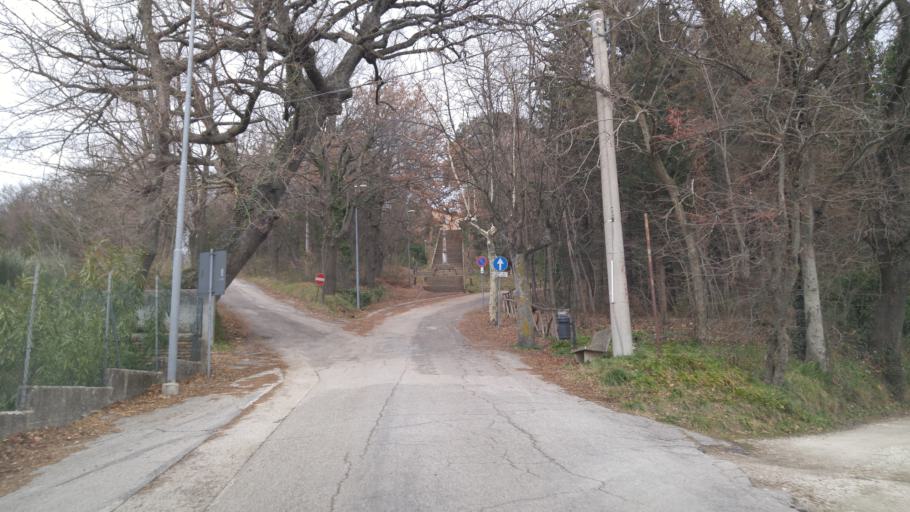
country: IT
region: The Marches
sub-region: Provincia di Pesaro e Urbino
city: Mombaroccio
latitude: 43.7888
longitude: 12.8600
